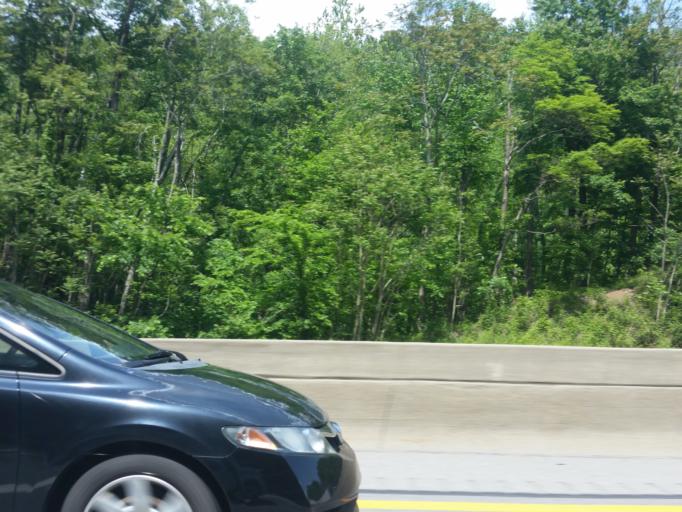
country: US
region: West Virginia
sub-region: Kanawha County
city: Montgomery
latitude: 38.0008
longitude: -81.3485
